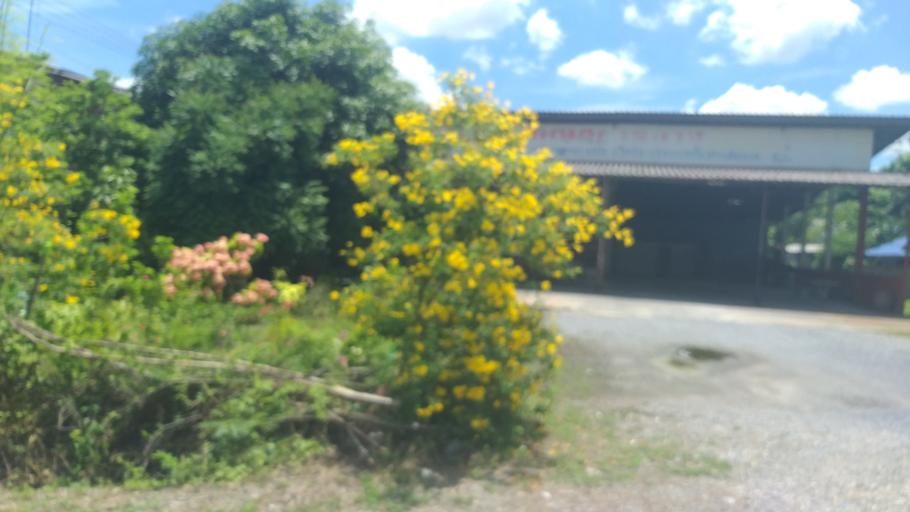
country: TH
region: Nakhon Nayok
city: Ban Na
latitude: 14.2675
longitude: 101.0655
